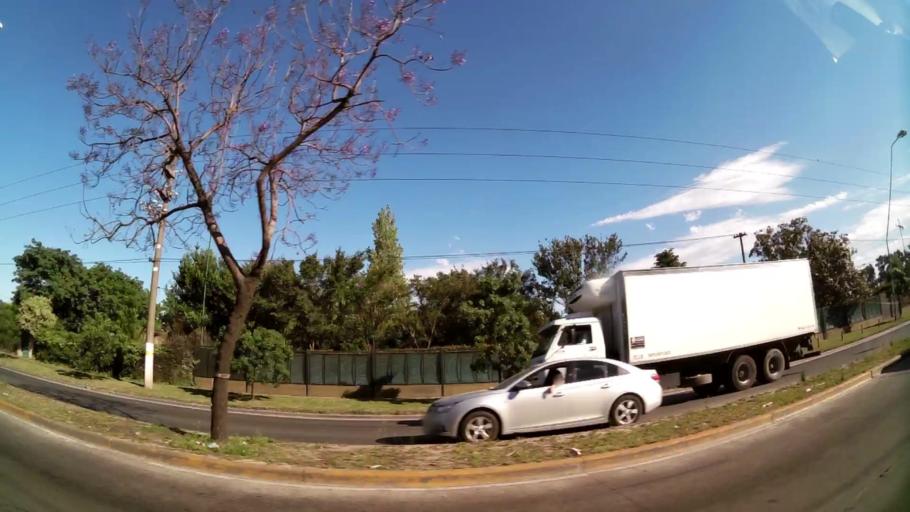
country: AR
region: Buenos Aires
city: Santa Catalina - Dique Lujan
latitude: -34.4811
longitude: -58.6783
